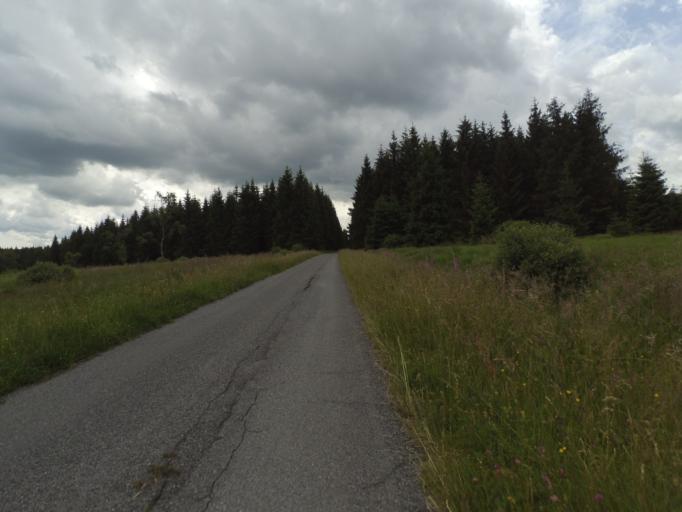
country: DE
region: North Rhine-Westphalia
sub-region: Regierungsbezirk Koln
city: Monschau
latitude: 50.5821
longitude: 6.1804
